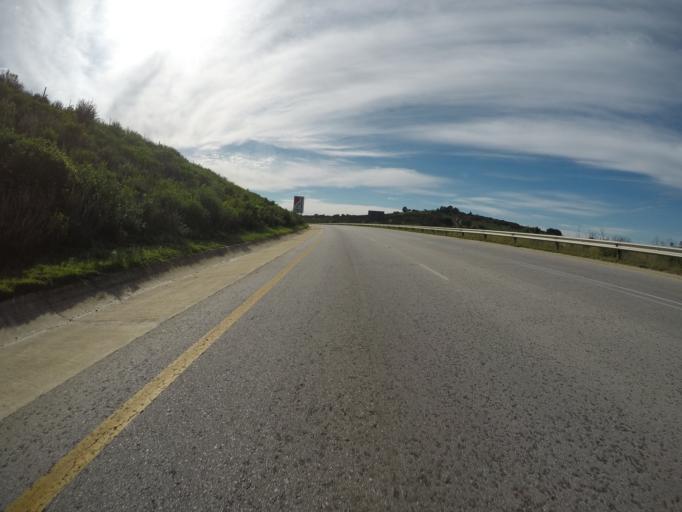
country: ZA
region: Eastern Cape
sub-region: Cacadu District Municipality
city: Jeffrey's Bay
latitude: -33.9028
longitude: 25.1102
